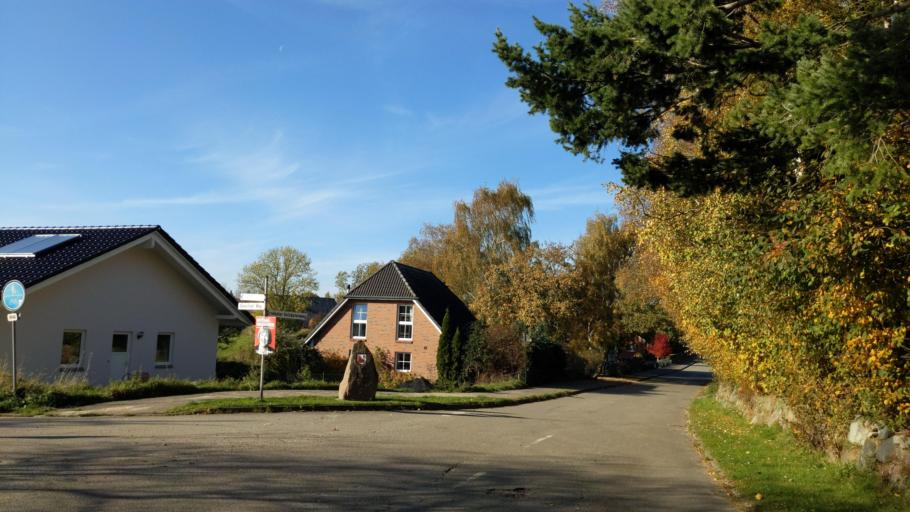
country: DE
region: Schleswig-Holstein
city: Kasseedorf
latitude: 54.1310
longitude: 10.7403
